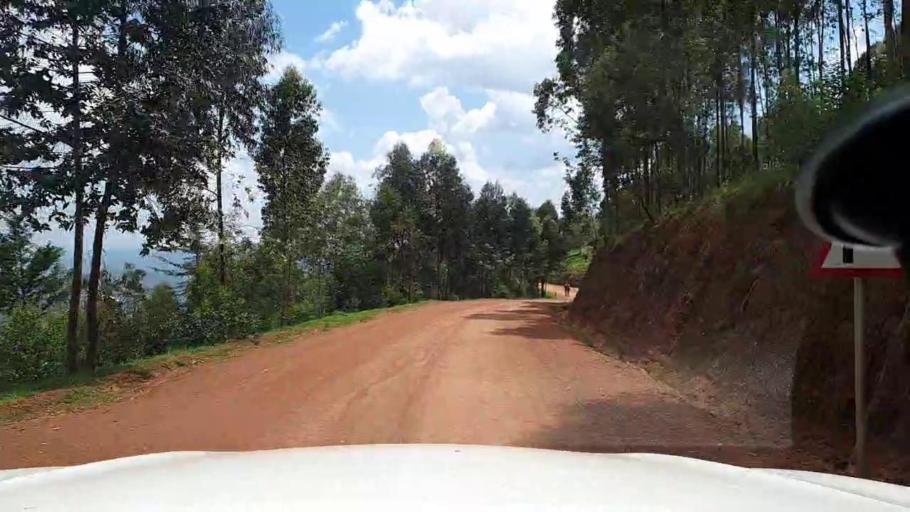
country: RW
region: Kigali
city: Kigali
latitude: -1.7885
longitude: 29.8439
